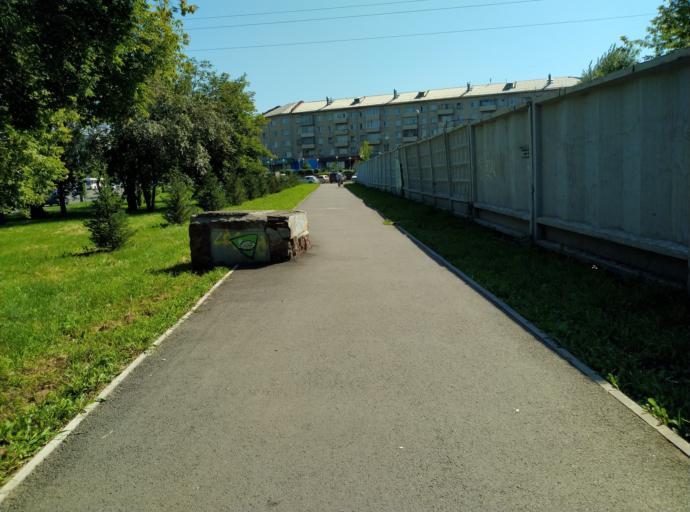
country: RU
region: Krasnoyarskiy
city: Krasnoyarsk
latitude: 56.0279
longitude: 92.7781
